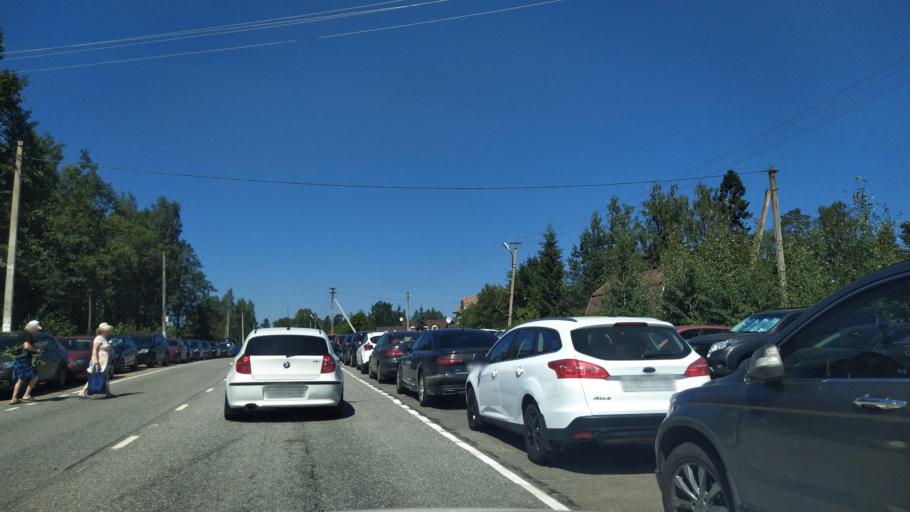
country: RU
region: Leningrad
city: Borisova Griva
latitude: 60.1173
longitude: 31.0795
